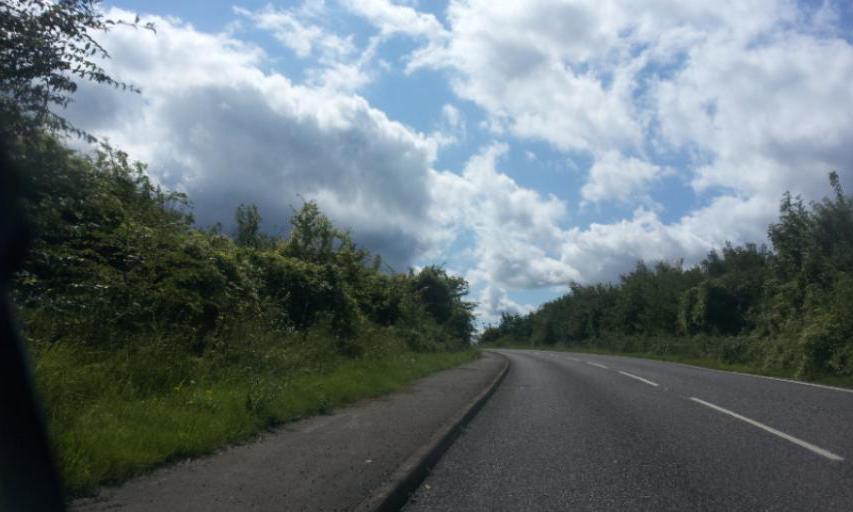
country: GB
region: England
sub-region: Kent
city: Boxley
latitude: 51.3276
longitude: 0.5615
